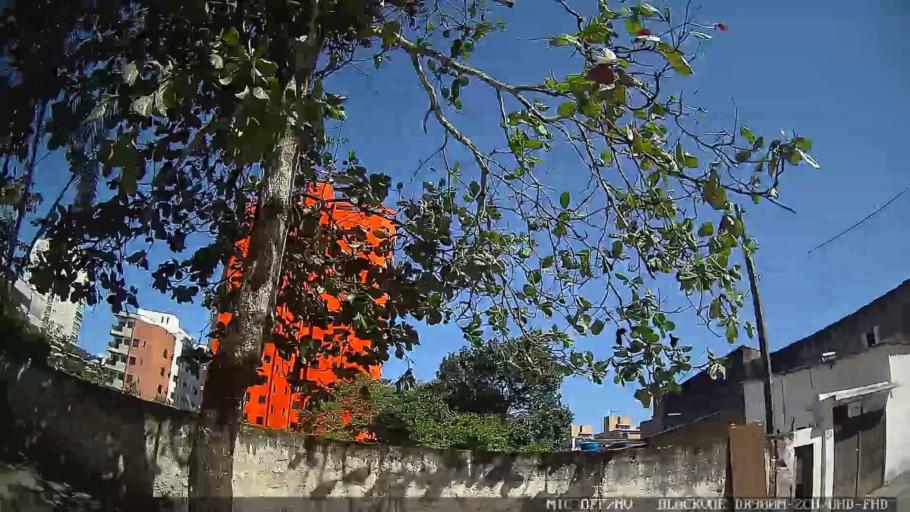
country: BR
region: Sao Paulo
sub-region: Guaruja
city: Guaruja
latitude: -23.9832
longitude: -46.2058
